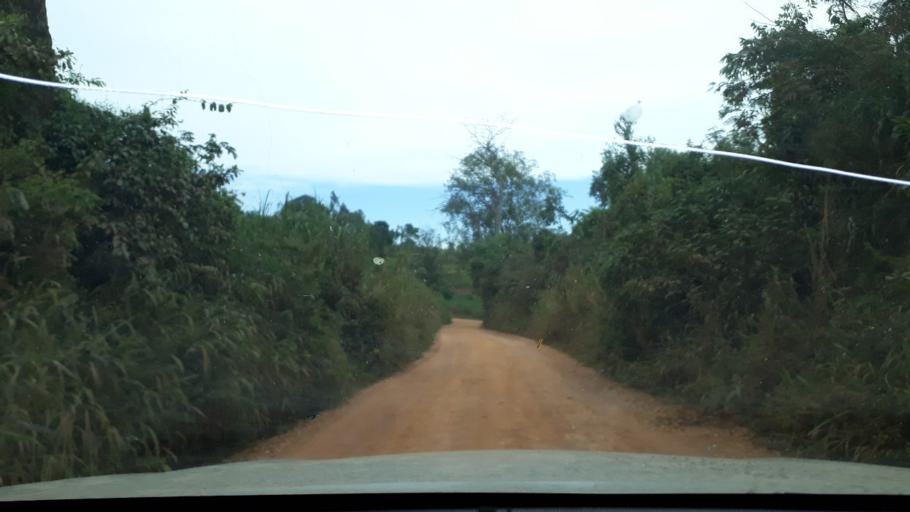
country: CD
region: Eastern Province
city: Bunia
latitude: 1.8475
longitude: 30.4715
